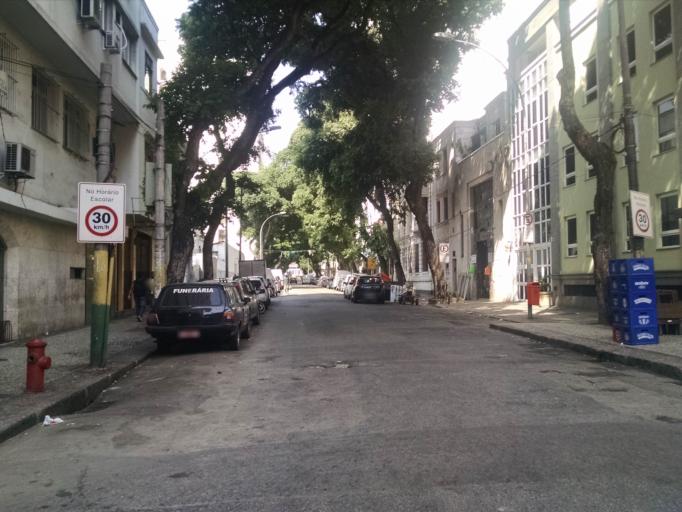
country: BR
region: Rio de Janeiro
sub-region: Rio De Janeiro
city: Rio de Janeiro
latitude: -22.9124
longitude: -43.1863
